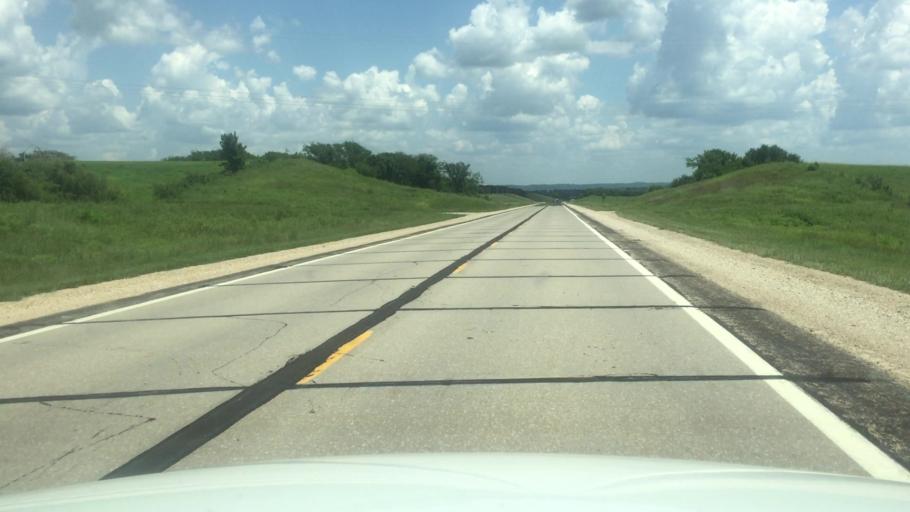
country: US
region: Kansas
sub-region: Atchison County
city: Atchison
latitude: 39.5571
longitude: -95.1775
